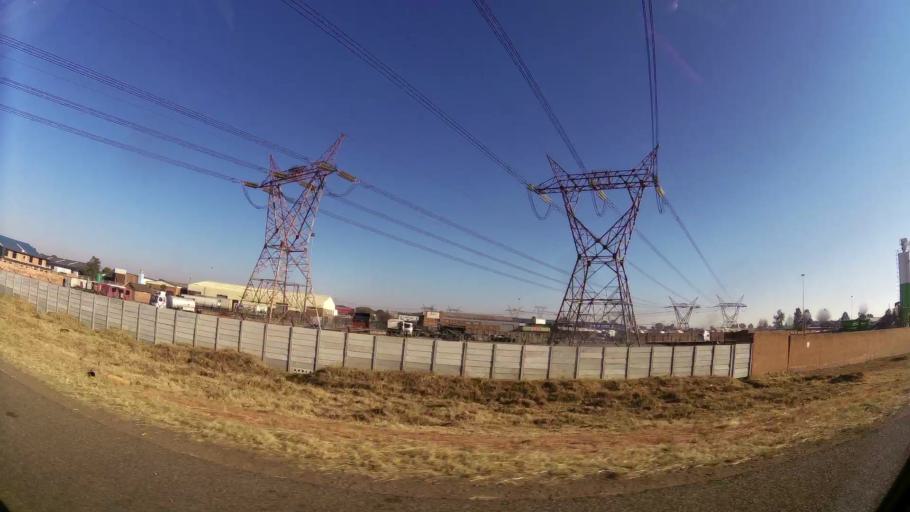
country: ZA
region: Gauteng
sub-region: Ekurhuleni Metropolitan Municipality
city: Germiston
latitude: -26.3572
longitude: 28.1209
